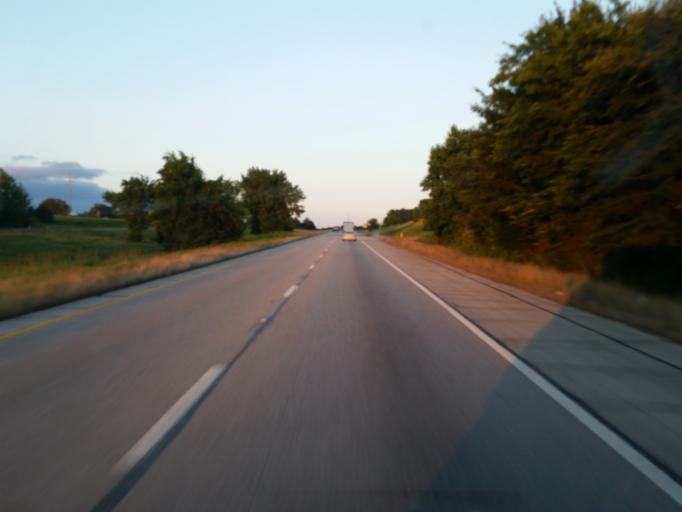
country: US
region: Texas
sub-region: Smith County
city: Hideaway
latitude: 32.4801
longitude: -95.4958
